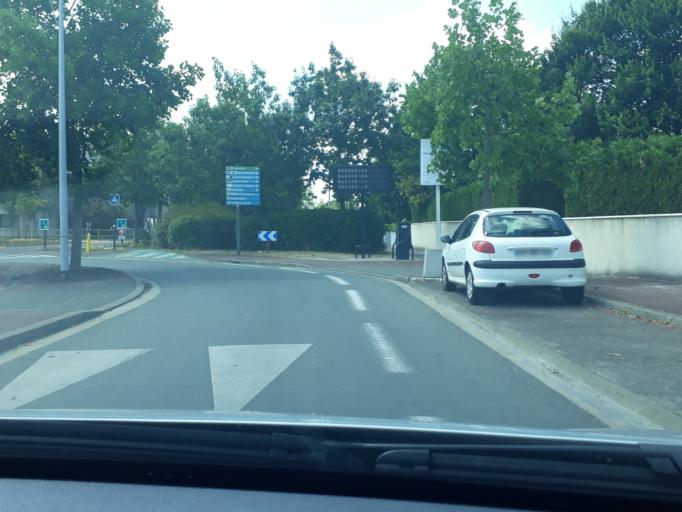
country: FR
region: Aquitaine
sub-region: Departement de la Gironde
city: Le Haillan
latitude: 44.8427
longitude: -0.6695
